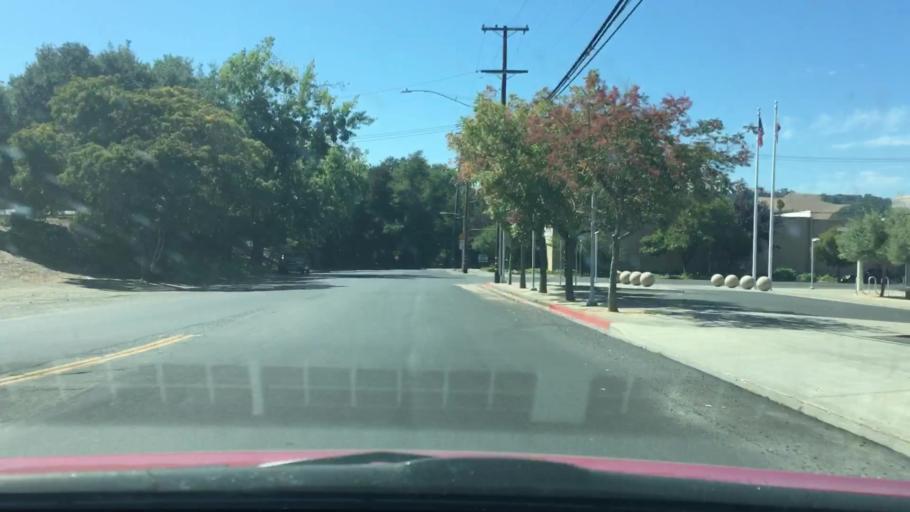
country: US
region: California
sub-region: Napa County
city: Napa
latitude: 38.2878
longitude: -122.2996
